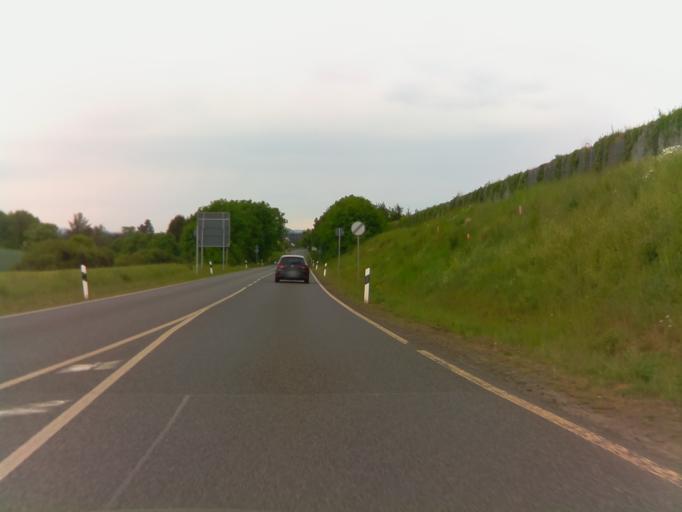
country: DE
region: Hesse
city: Stadtallendorf
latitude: 50.8344
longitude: 9.0263
